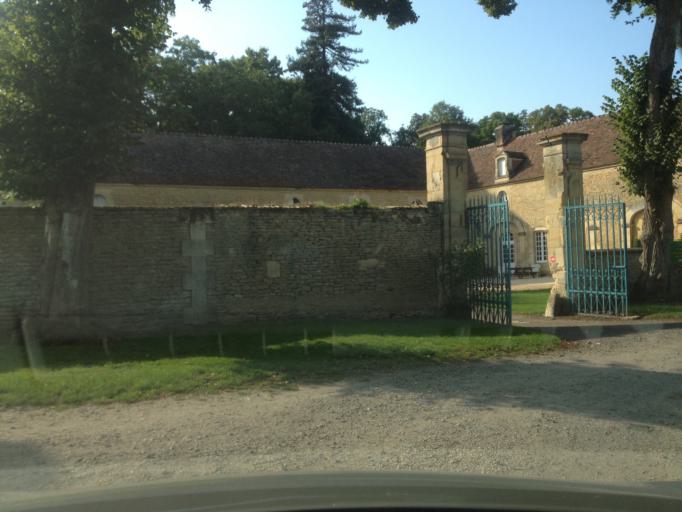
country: FR
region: Lower Normandy
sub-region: Departement du Calvados
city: Canon
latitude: 49.0791
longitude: -0.0941
